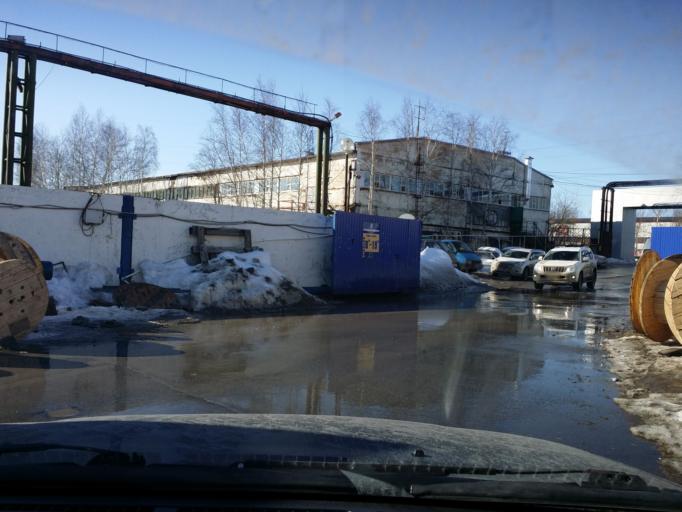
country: RU
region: Khanty-Mansiyskiy Avtonomnyy Okrug
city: Nizhnevartovsk
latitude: 60.9440
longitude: 76.5341
